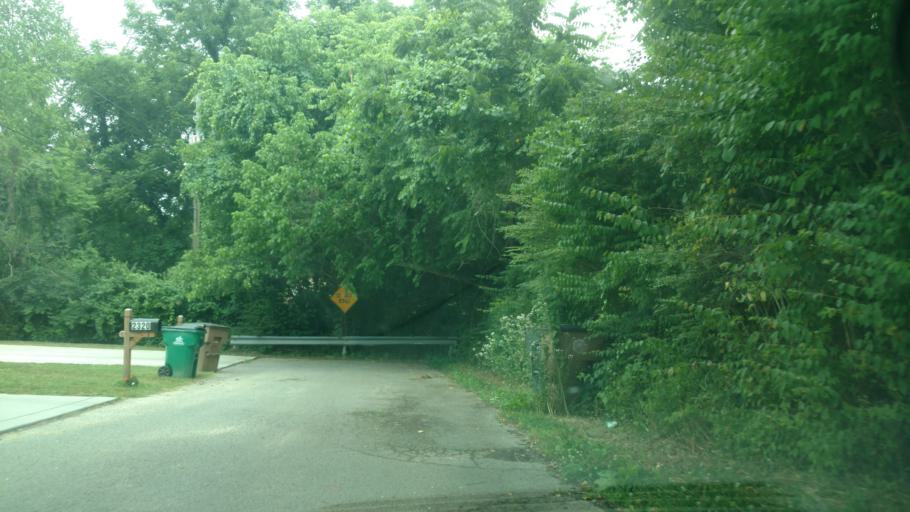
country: US
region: Tennessee
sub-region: Davidson County
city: Nashville
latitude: 36.2073
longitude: -86.7215
